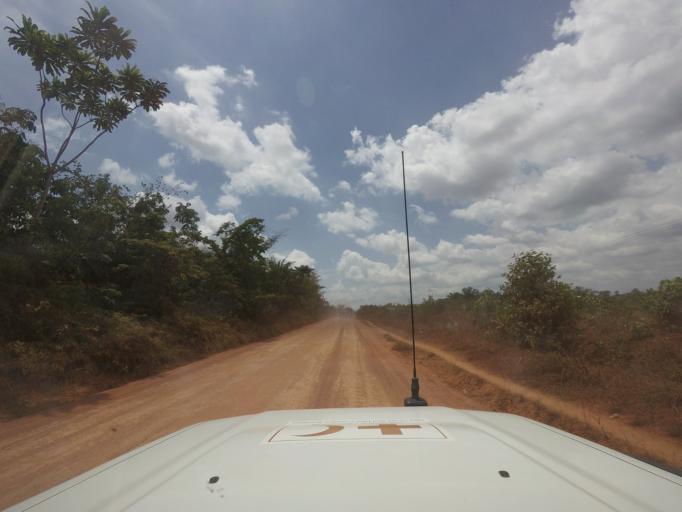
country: LR
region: Nimba
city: Sanniquellie
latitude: 7.2306
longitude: -8.9522
